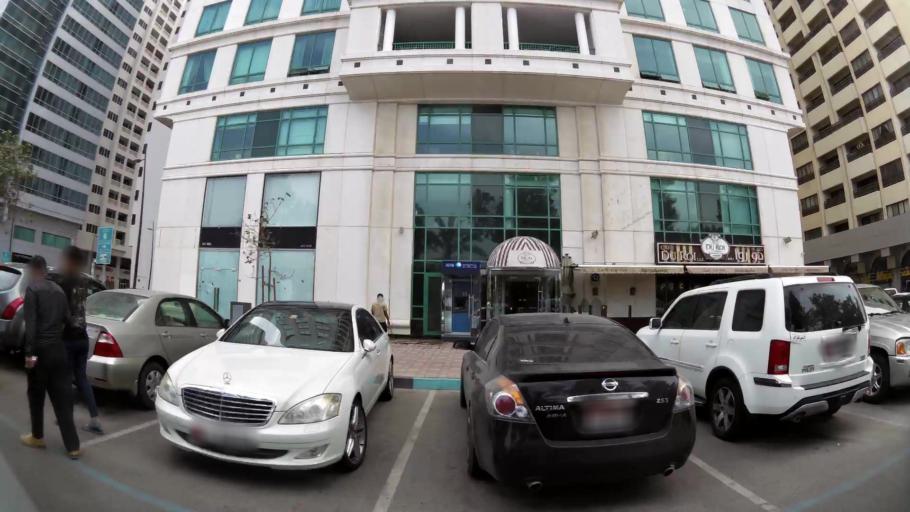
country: AE
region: Abu Dhabi
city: Abu Dhabi
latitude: 24.4714
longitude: 54.3397
